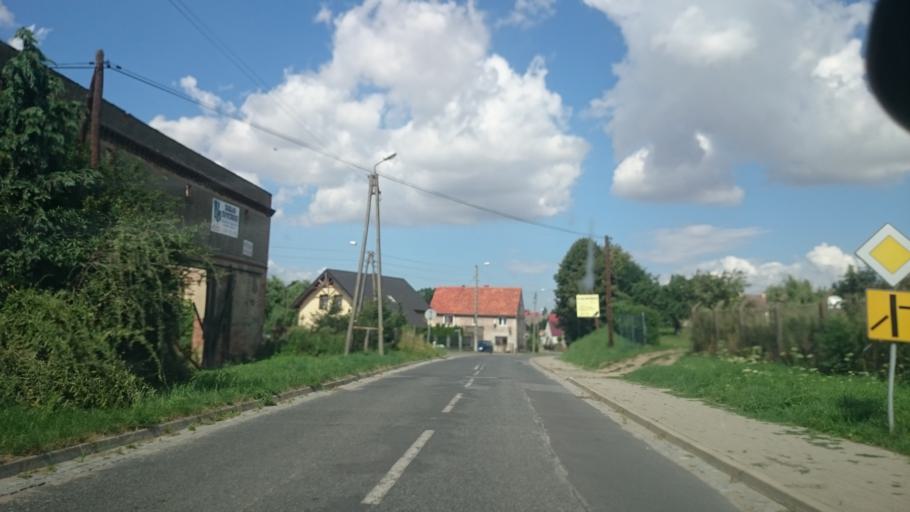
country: PL
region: Lower Silesian Voivodeship
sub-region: Powiat zabkowicki
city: Zabkowice Slaskie
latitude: 50.5798
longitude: 16.8284
